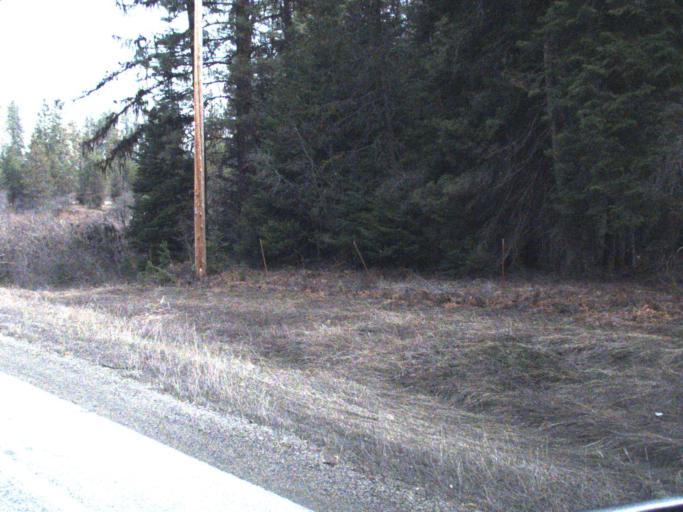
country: US
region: Washington
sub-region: Pend Oreille County
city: Newport
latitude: 48.2715
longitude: -117.2613
